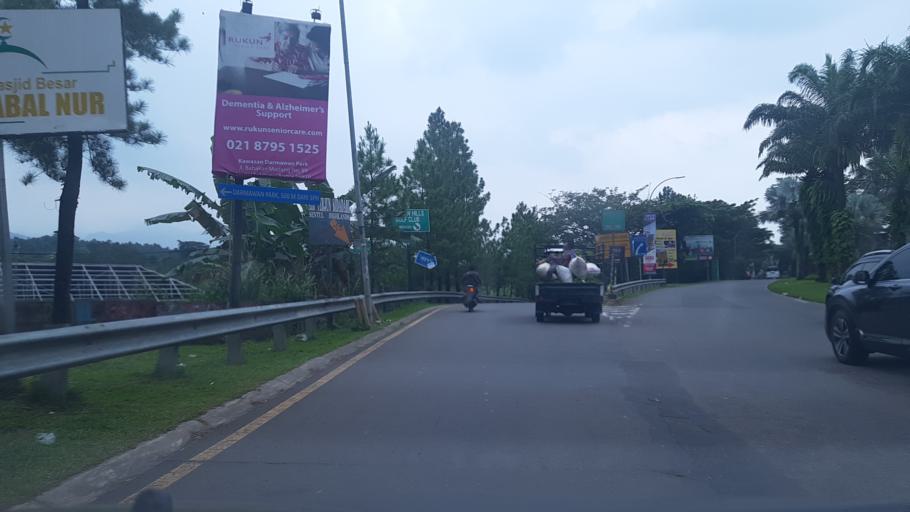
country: ID
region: West Java
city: Bogor
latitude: -6.5713
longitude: 106.8630
